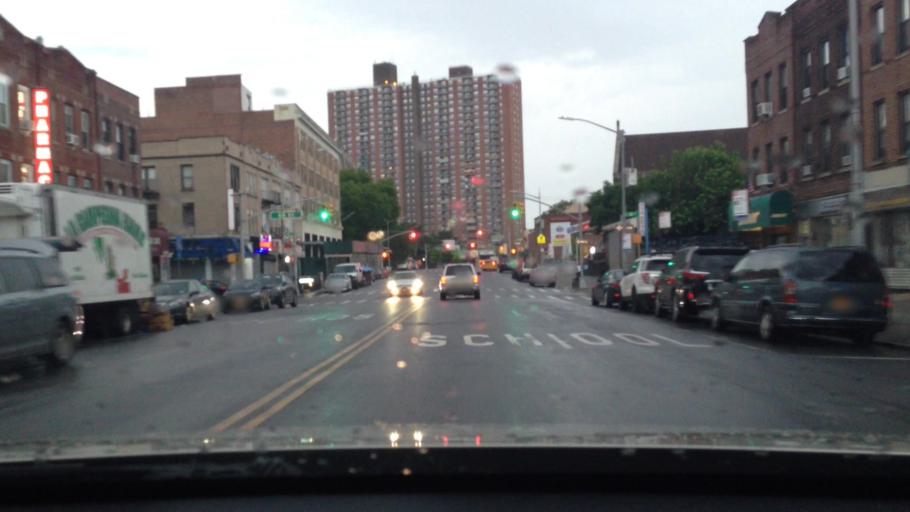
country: US
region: New York
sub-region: Kings County
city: Bensonhurst
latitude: 40.6348
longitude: -74.0234
